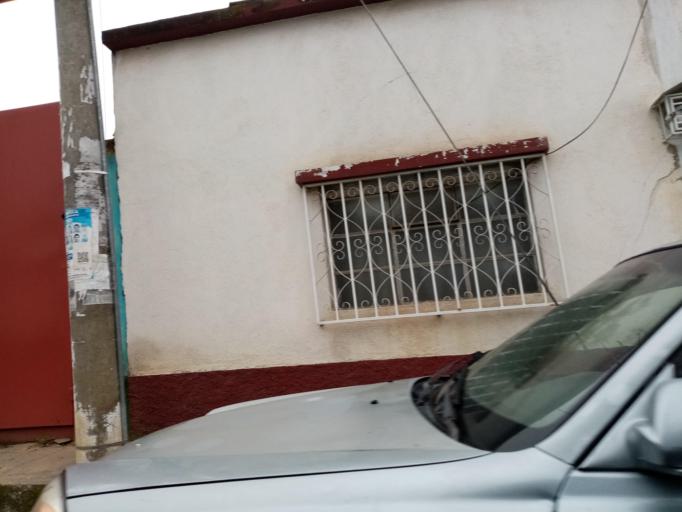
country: GT
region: Quetzaltenango
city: Quetzaltenango
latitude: 14.8511
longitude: -91.5156
